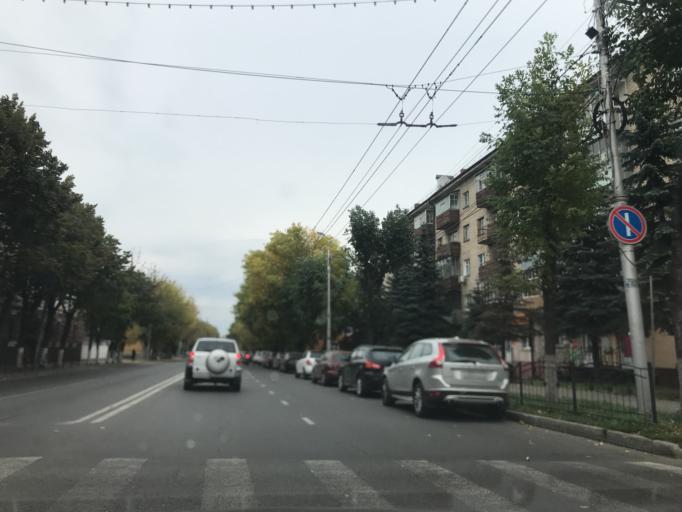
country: RU
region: Kaluga
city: Kaluga
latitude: 54.5156
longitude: 36.2652
